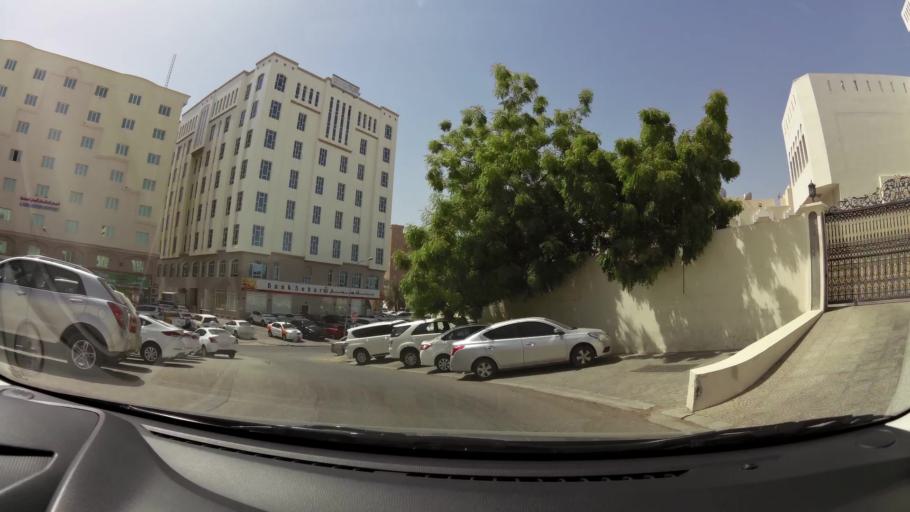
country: OM
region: Muhafazat Masqat
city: Bawshar
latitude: 23.5939
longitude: 58.4263
